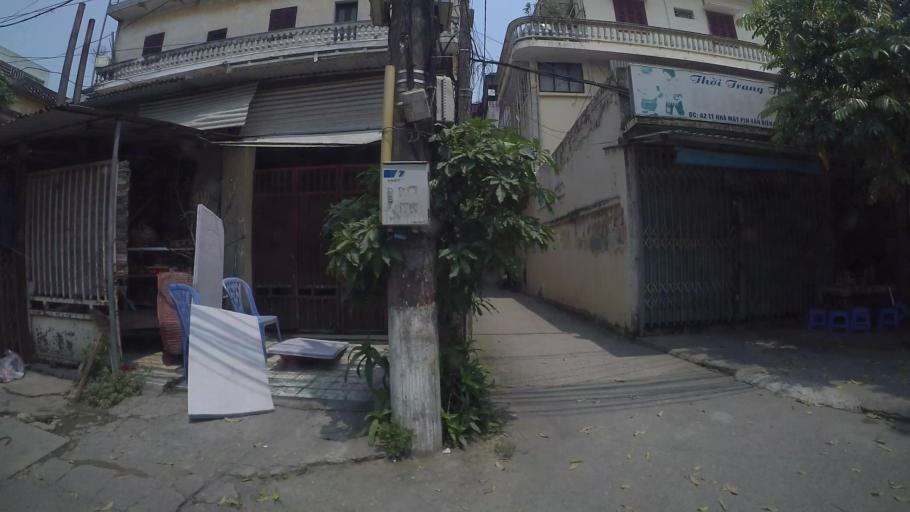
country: VN
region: Ha Noi
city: Van Dien
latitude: 20.9446
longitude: 105.8419
